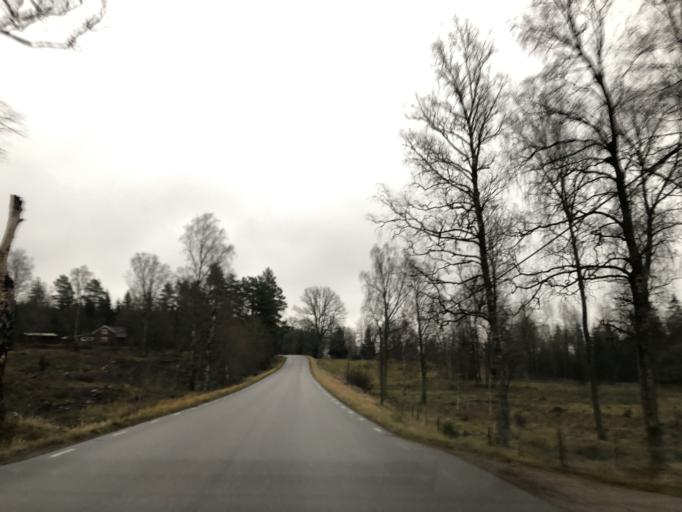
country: SE
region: Vaestra Goetaland
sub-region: Ulricehamns Kommun
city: Ulricehamn
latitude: 57.8500
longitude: 13.2583
